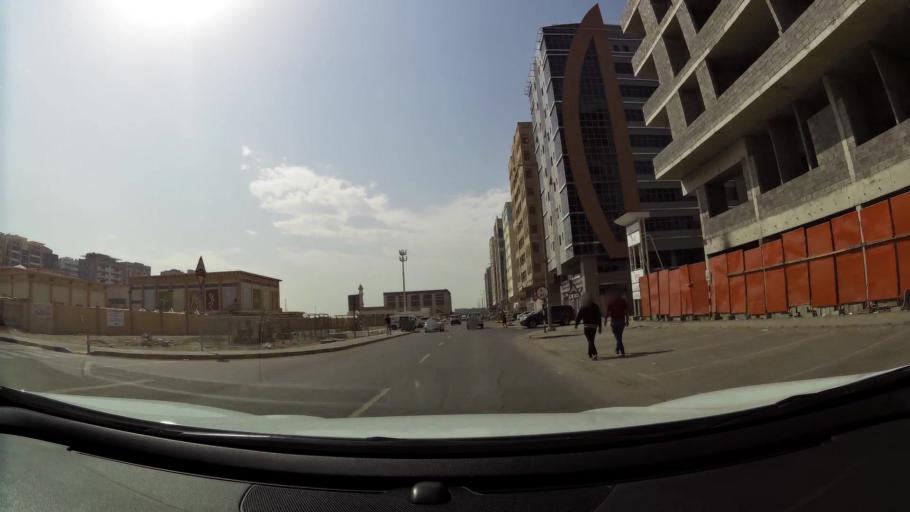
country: AE
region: Abu Dhabi
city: Abu Dhabi
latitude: 24.3434
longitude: 54.5336
